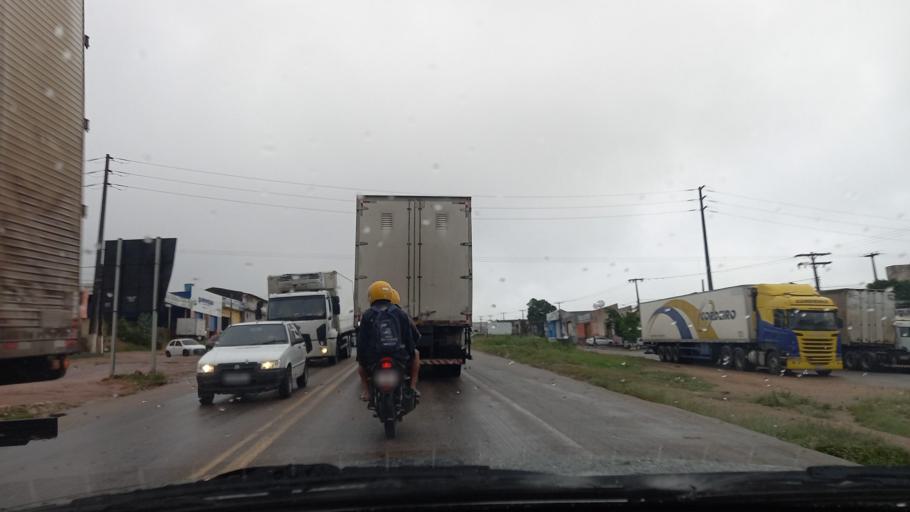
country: BR
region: Pernambuco
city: Garanhuns
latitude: -8.8809
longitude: -36.4920
